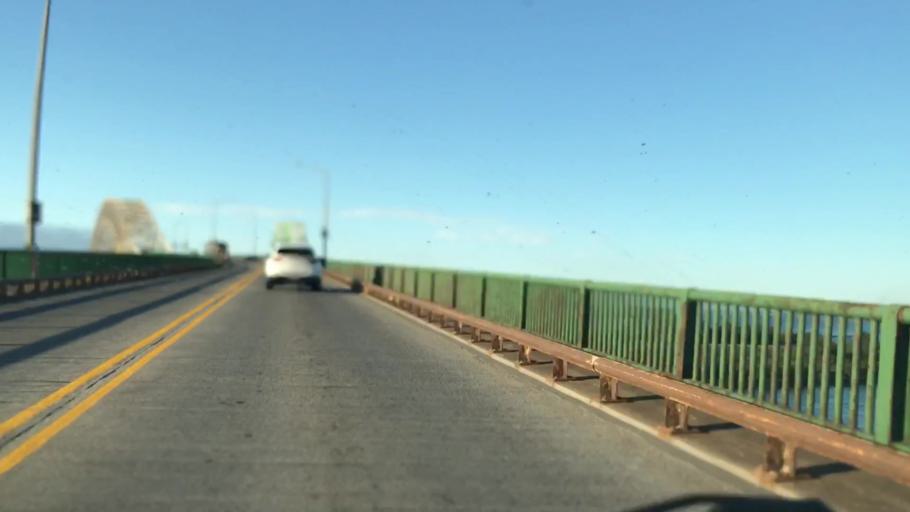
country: CA
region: Ontario
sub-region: Algoma
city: Sault Ste. Marie
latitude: 46.5164
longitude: -84.3569
